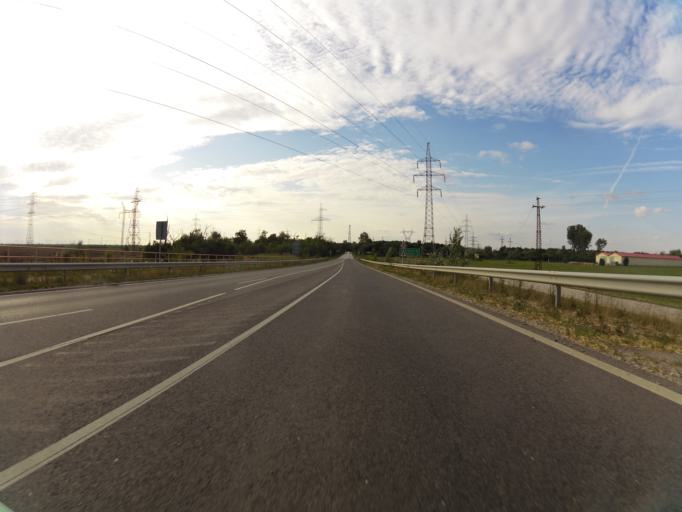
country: HU
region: Csongrad
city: Szeged
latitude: 46.2973
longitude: 20.1338
